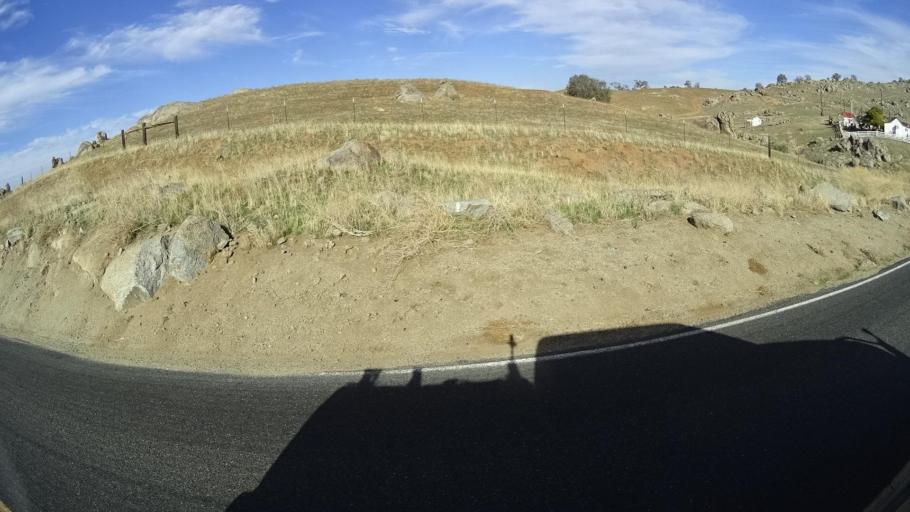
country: US
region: California
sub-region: Kern County
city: Oildale
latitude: 35.6121
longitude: -118.8599
